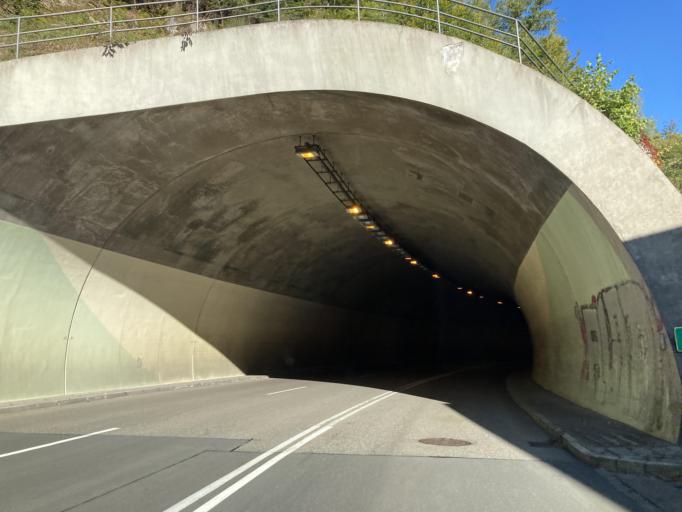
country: DE
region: Baden-Wuerttemberg
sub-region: Freiburg Region
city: Triberg im Schwarzwald
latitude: 48.1619
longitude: 8.2365
